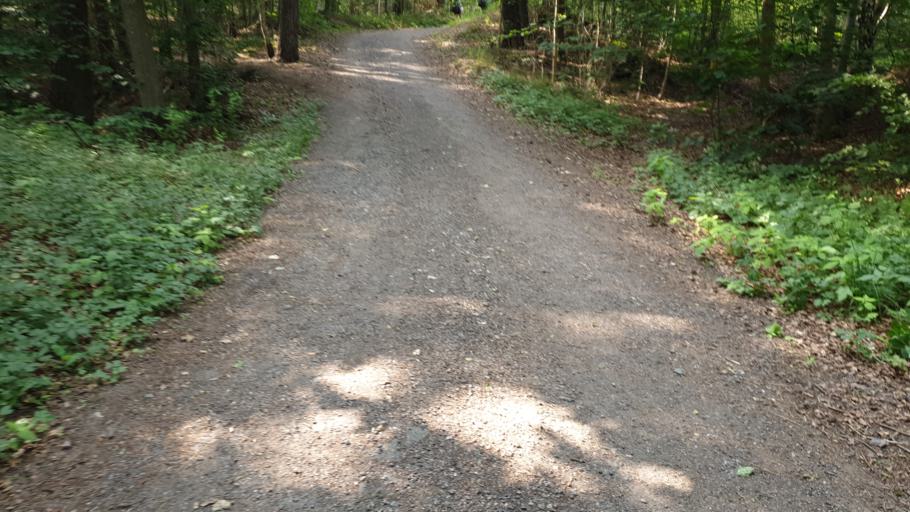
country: SE
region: Vaestra Goetaland
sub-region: Molndal
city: Moelndal
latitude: 57.6662
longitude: 12.0451
